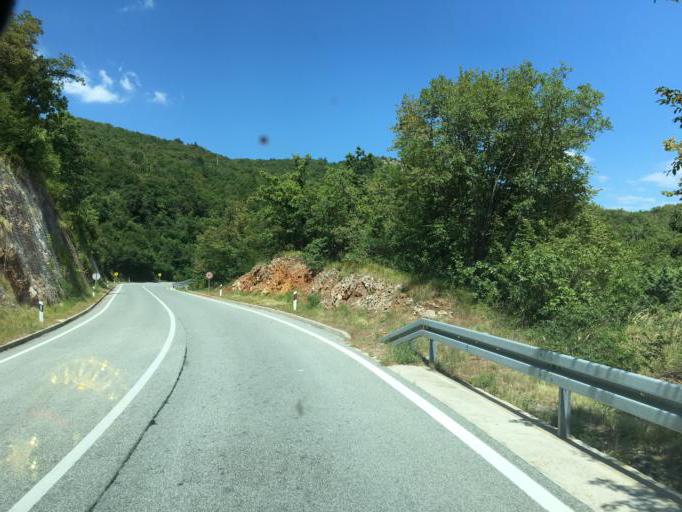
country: HR
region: Istarska
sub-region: Grad Labin
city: Rabac
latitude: 45.1358
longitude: 14.2061
